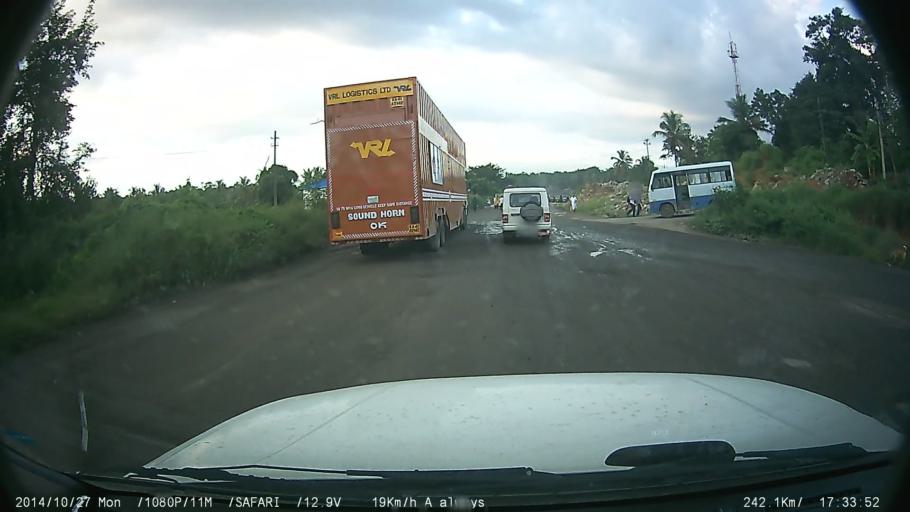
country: IN
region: Kerala
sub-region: Palakkad district
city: Palakkad
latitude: 10.6835
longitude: 76.5790
